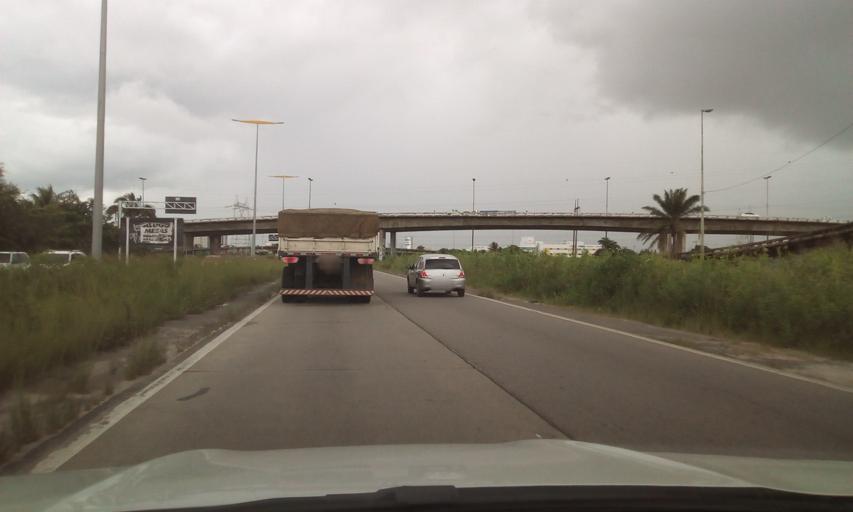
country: BR
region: Pernambuco
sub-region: Recife
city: Recife
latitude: -8.0655
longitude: -34.9431
